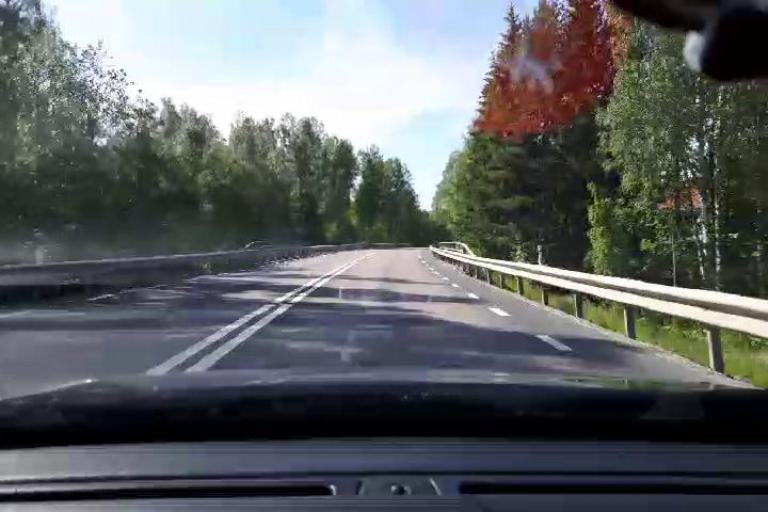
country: SE
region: Gaevleborg
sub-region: Soderhamns Kommun
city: Soderhamn
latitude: 61.1661
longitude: 16.8288
